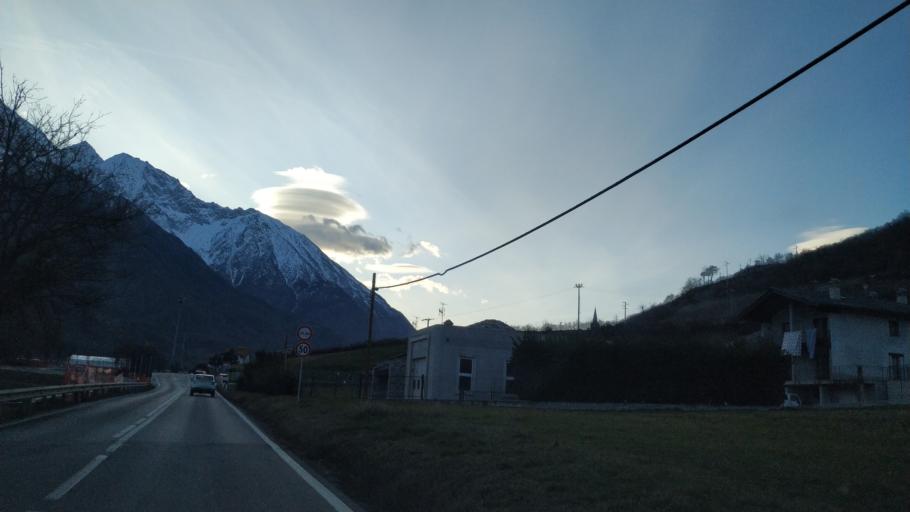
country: IT
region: Aosta Valley
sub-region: Valle d'Aosta
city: Nus
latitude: 45.7431
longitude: 7.4775
